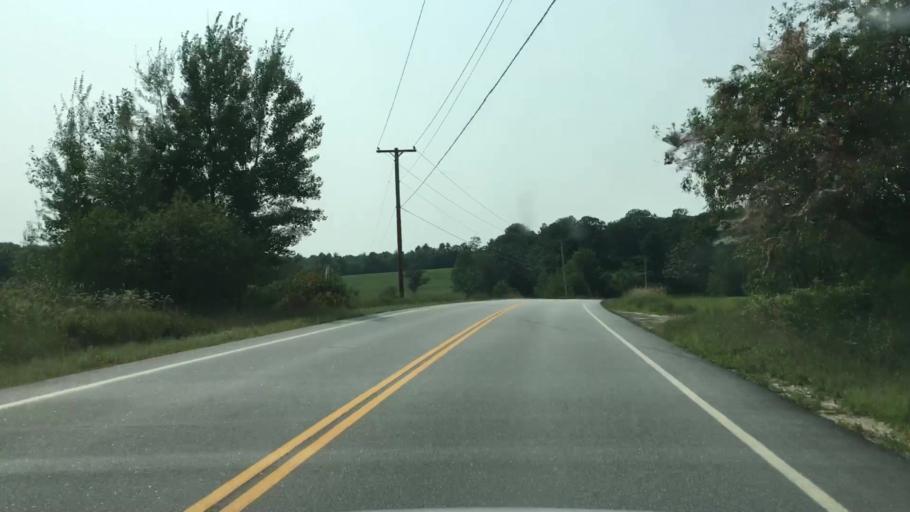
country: US
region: Maine
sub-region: Androscoggin County
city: Livermore
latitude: 44.3288
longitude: -70.2803
